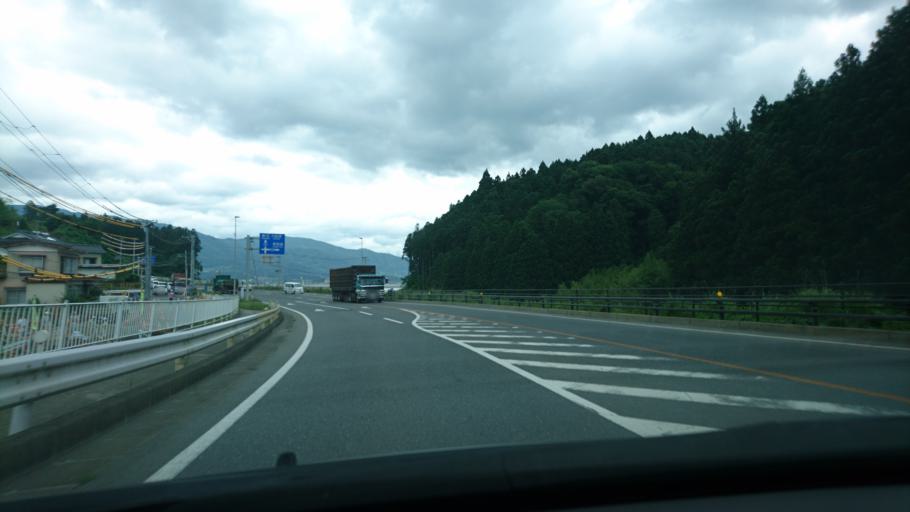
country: JP
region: Iwate
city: Ofunato
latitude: 38.9960
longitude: 141.6208
